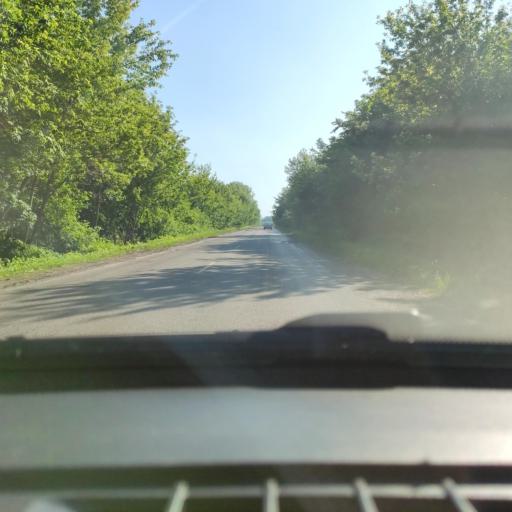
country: RU
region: Voronezj
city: Panino
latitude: 51.6150
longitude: 40.0113
